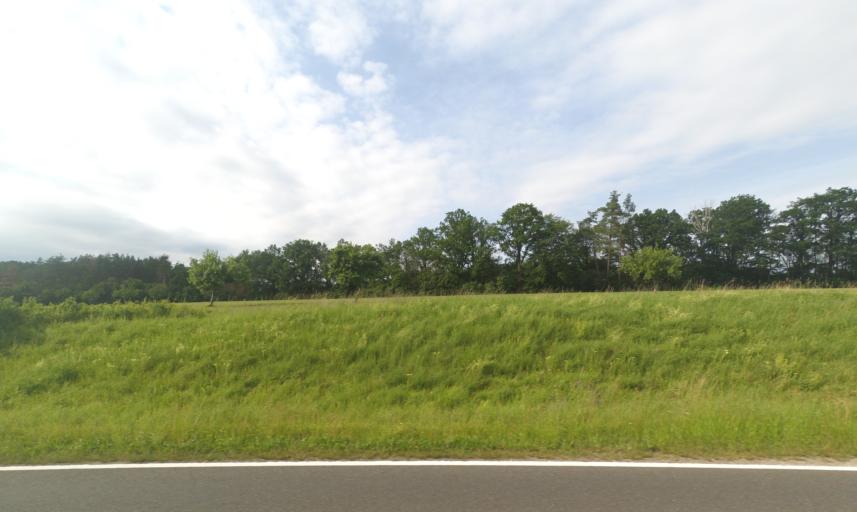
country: DE
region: Bavaria
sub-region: Regierungsbezirk Mittelfranken
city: Wachenroth
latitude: 49.7864
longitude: 10.6897
